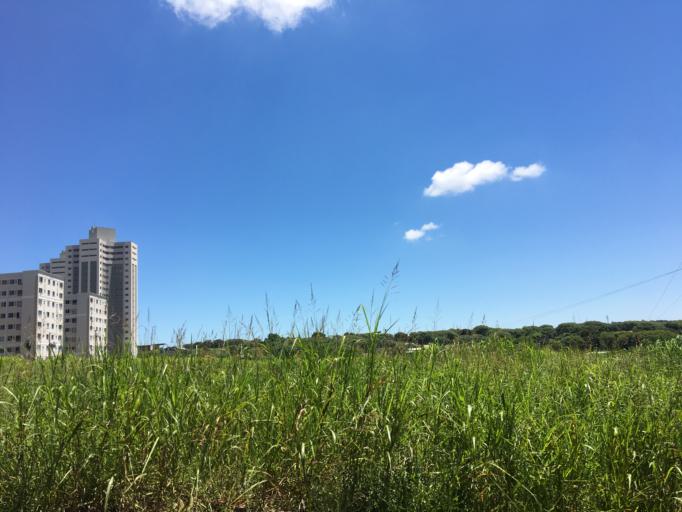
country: BR
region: Parana
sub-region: Maringa
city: Maringa
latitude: -23.4479
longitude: -51.9783
